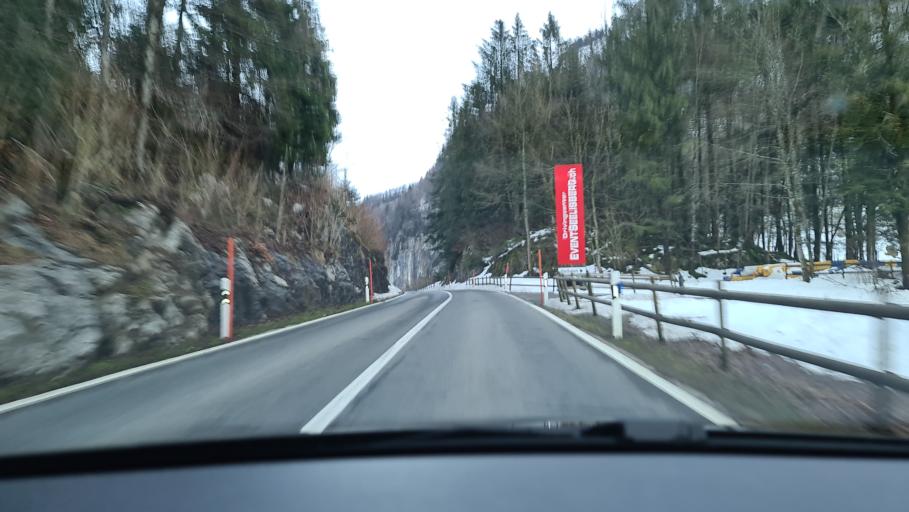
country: CH
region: Uri
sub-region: Uri
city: Bauen
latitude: 46.9592
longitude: 8.5583
